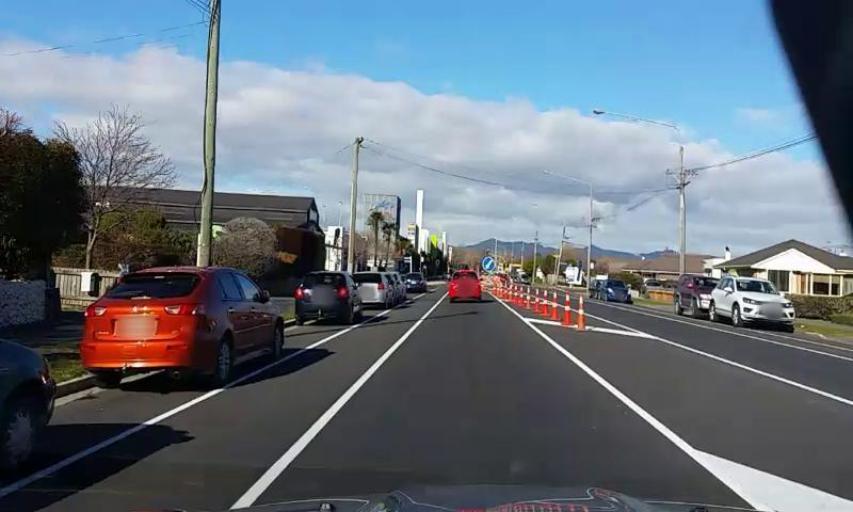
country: NZ
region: Canterbury
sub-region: Christchurch City
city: Christchurch
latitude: -43.5043
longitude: 172.6625
